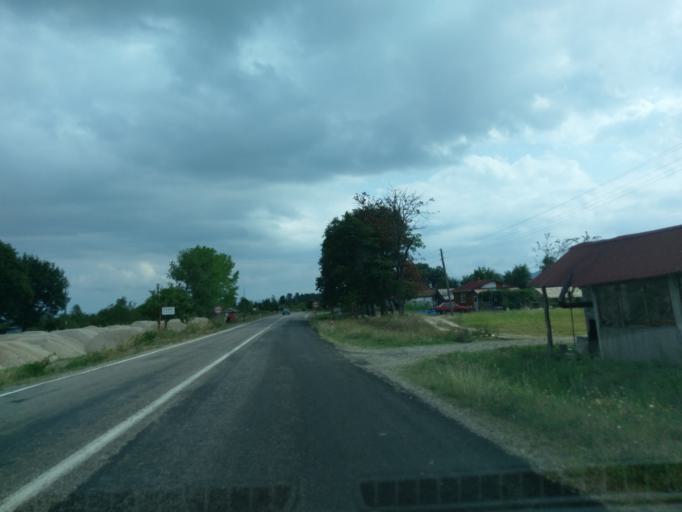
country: TR
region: Sinop
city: Yenikonak
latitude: 41.9485
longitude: 34.7625
